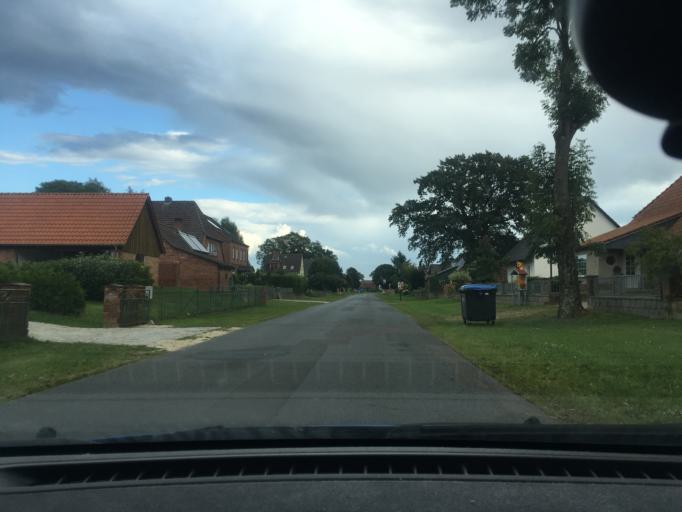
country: DE
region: Lower Saxony
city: Neu Darchau
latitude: 53.3445
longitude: 10.8528
